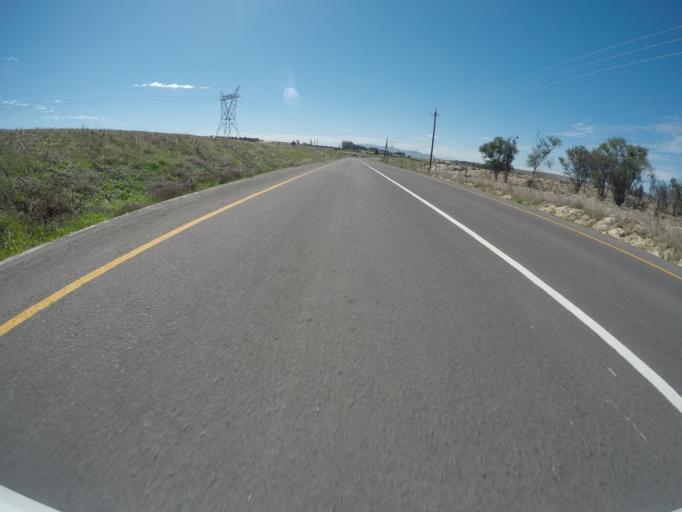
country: ZA
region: Western Cape
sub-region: West Coast District Municipality
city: Malmesbury
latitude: -33.5144
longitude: 18.6562
